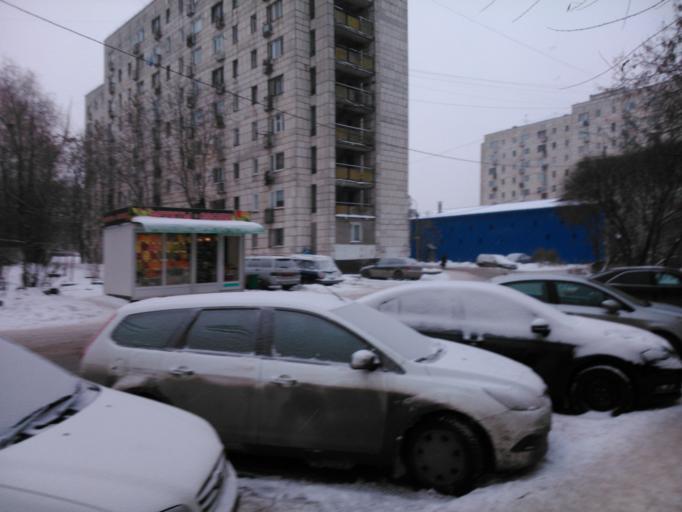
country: RU
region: Perm
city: Perm
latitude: 57.9887
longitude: 56.2430
